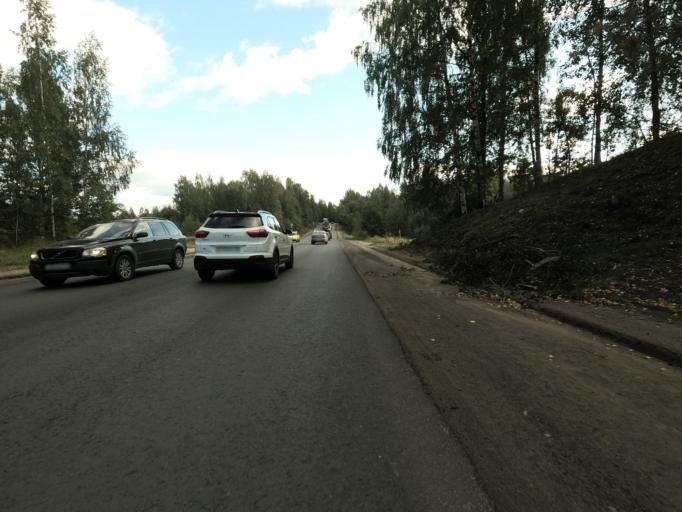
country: RU
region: Leningrad
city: Koltushi
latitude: 59.9688
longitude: 30.6557
